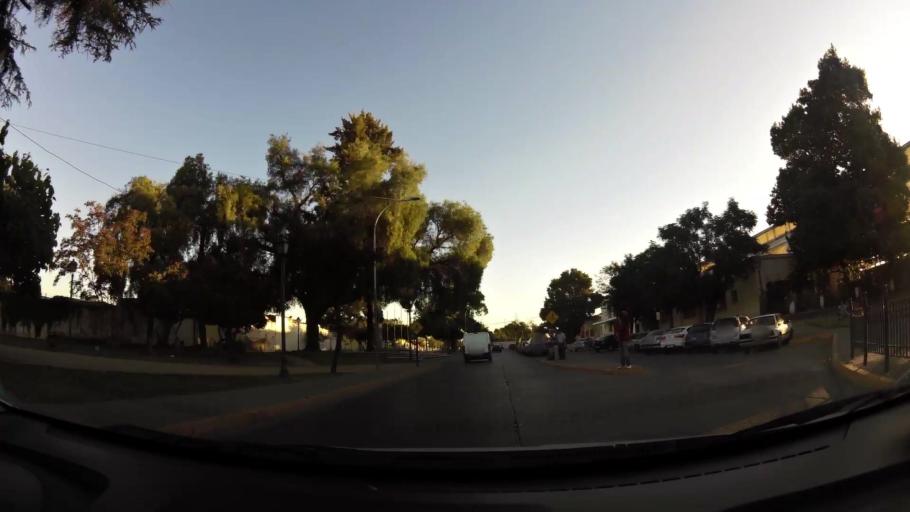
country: CL
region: O'Higgins
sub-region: Provincia de Cachapoal
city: Rancagua
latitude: -34.1700
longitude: -70.7524
